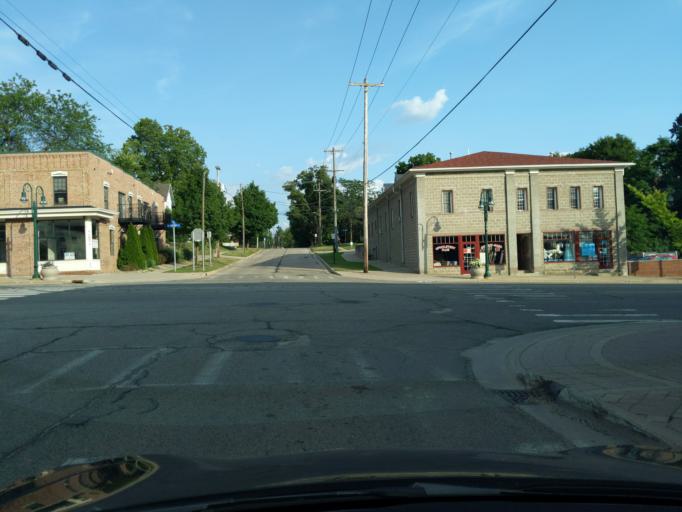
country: US
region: Michigan
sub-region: Eaton County
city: Grand Ledge
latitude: 42.7561
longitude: -84.7419
